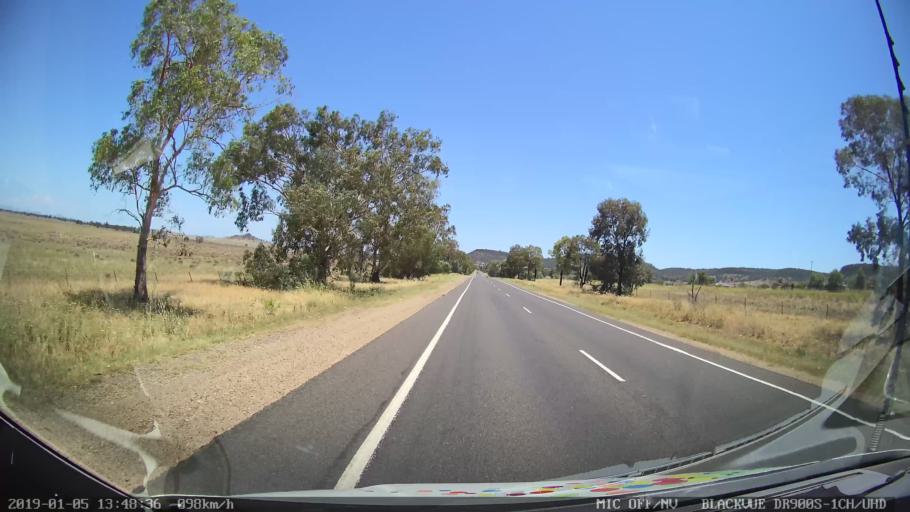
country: AU
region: New South Wales
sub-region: Gunnedah
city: Gunnedah
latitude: -31.0041
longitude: 150.2772
